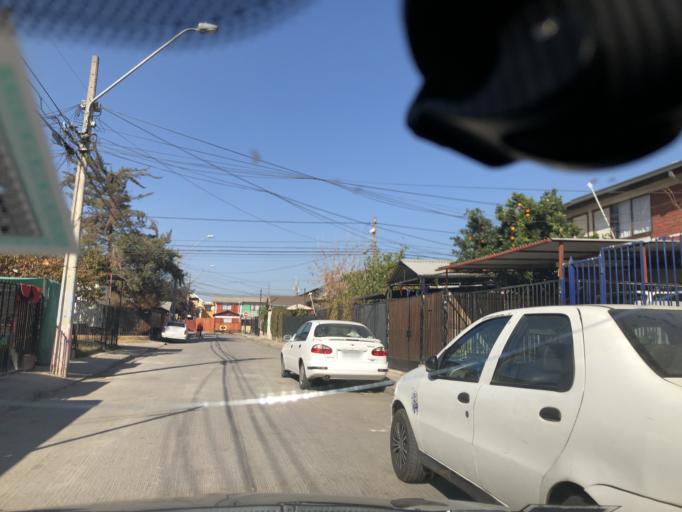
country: CL
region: Santiago Metropolitan
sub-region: Provincia de Cordillera
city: Puente Alto
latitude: -33.5831
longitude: -70.5887
